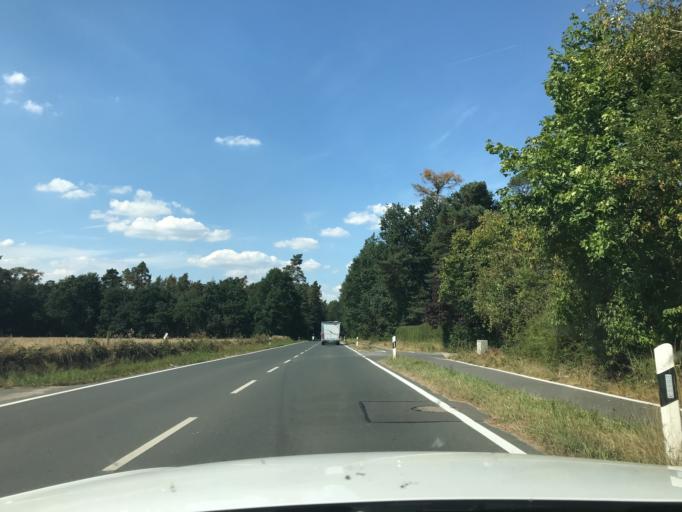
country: DE
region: Bavaria
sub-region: Regierungsbezirk Mittelfranken
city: Erlangen
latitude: 49.5563
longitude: 11.0160
